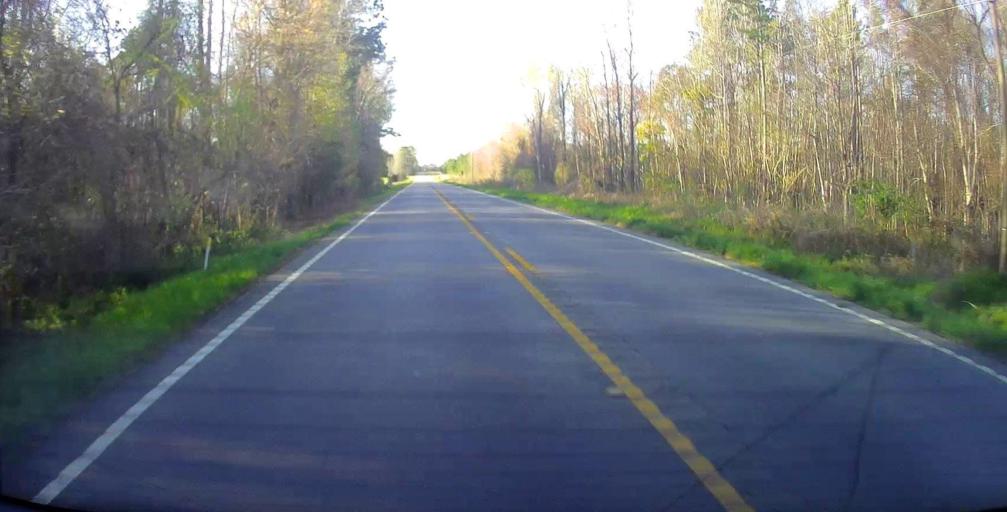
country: US
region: Georgia
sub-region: Pulaski County
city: Hawkinsville
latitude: 32.2239
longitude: -83.3905
